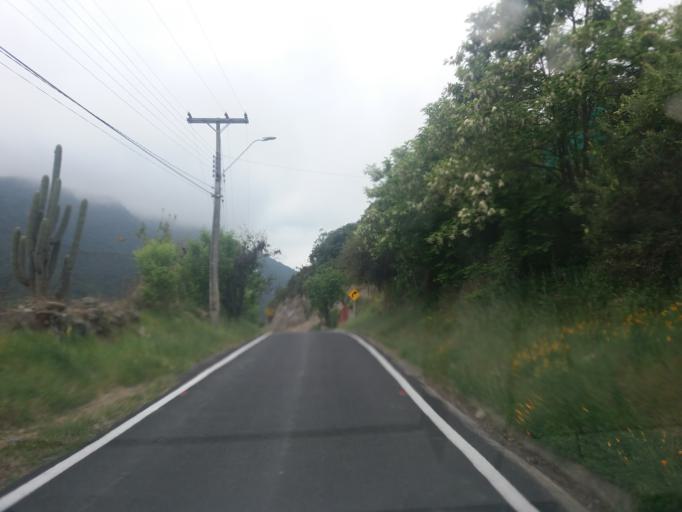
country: CL
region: Valparaiso
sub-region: Provincia de Marga Marga
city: Limache
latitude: -33.0441
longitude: -71.0990
